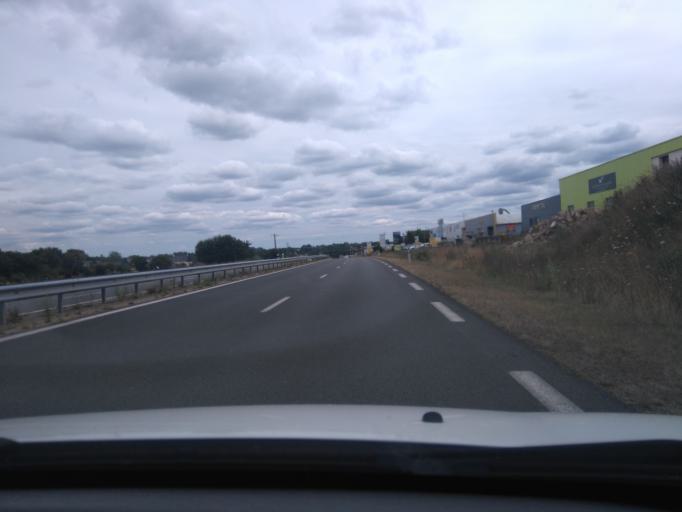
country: FR
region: Brittany
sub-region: Departement des Cotes-d'Armor
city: Cavan
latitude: 48.6880
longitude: -3.3662
